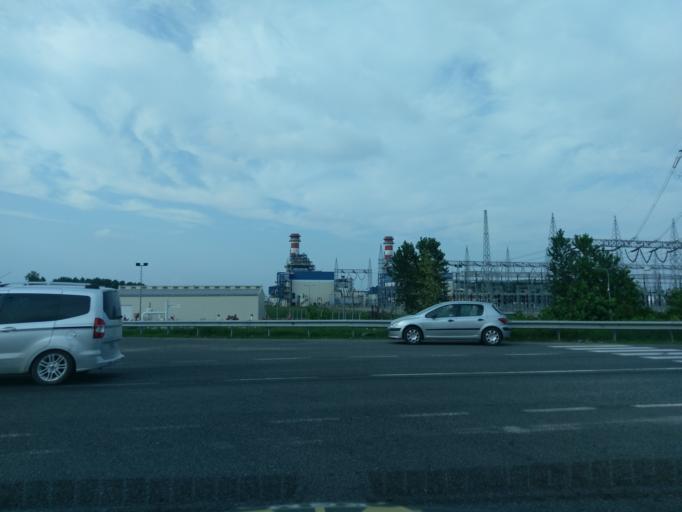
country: TR
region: Ordu
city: Ikizce
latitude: 41.1418
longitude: 37.1547
